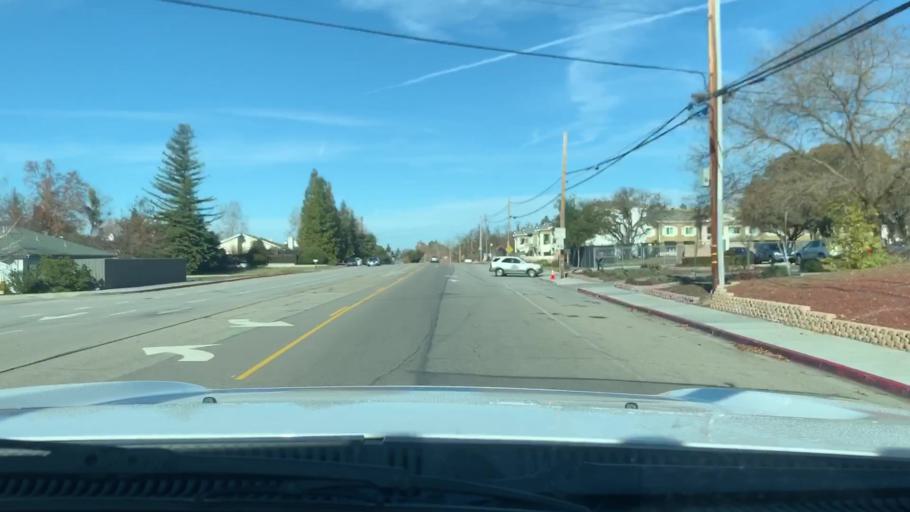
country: US
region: California
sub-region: San Luis Obispo County
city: Atascadero
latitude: 35.4564
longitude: -120.6406
